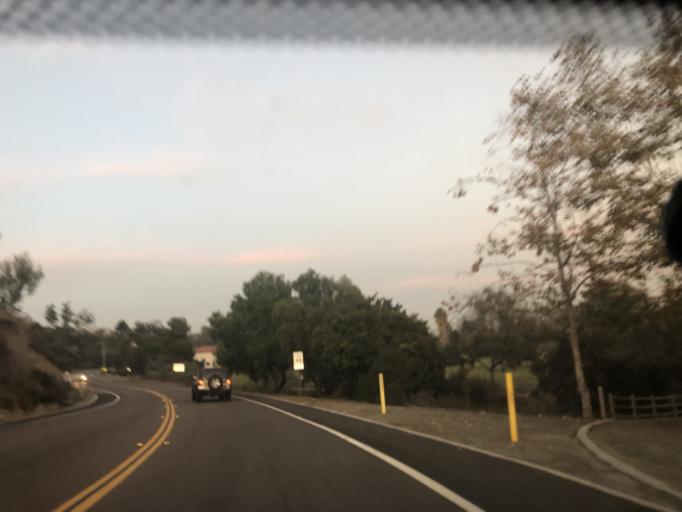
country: US
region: California
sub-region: San Diego County
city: Bonita
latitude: 32.6601
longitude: -117.0435
